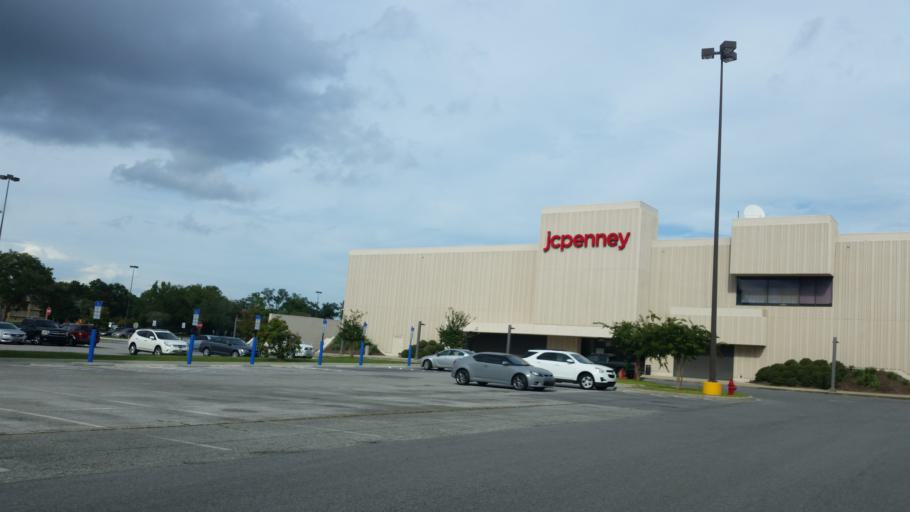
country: US
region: Florida
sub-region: Escambia County
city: Ferry Pass
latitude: 30.4999
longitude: -87.2257
